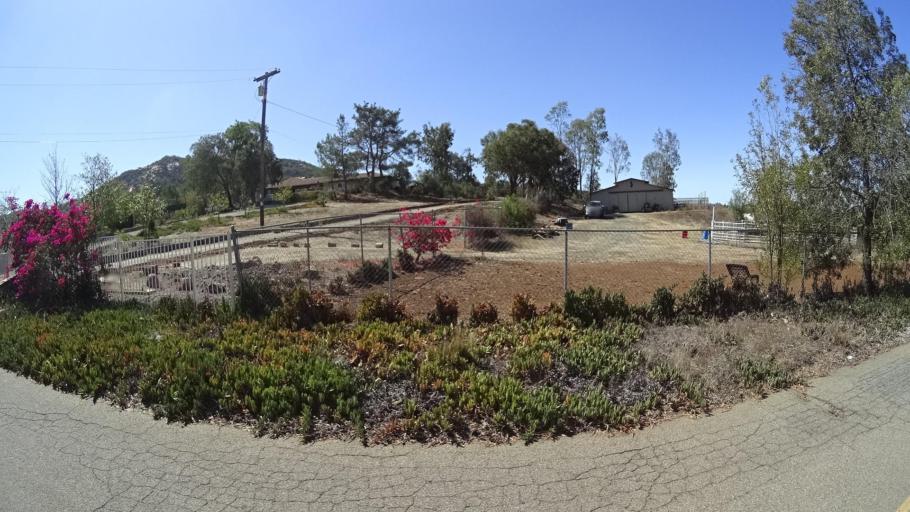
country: US
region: California
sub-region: San Diego County
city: Rainbow
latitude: 33.4294
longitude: -117.1681
